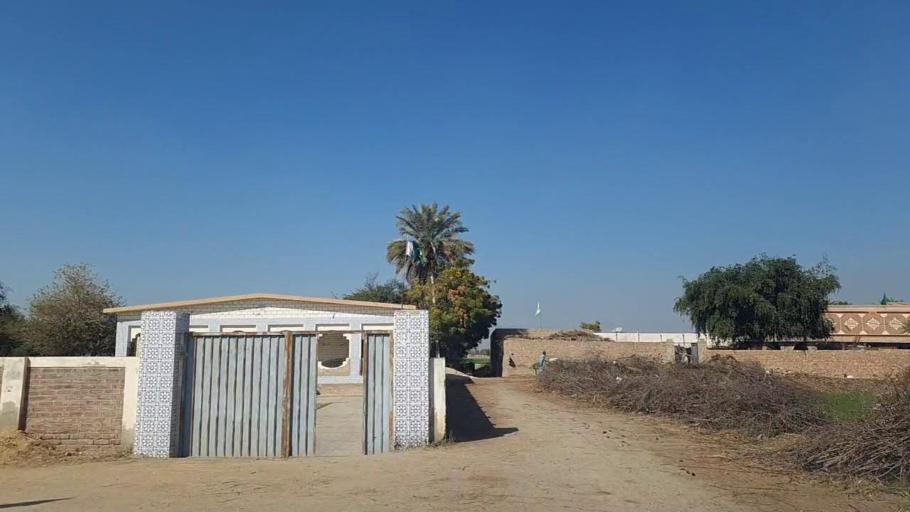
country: PK
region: Sindh
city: Jam Sahib
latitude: 26.2246
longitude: 68.6072
